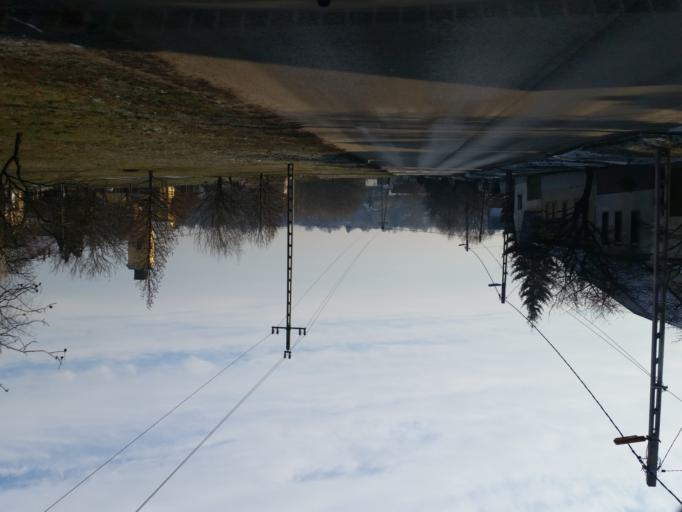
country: HU
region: Pest
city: Biatorbagy
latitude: 47.4796
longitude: 18.8323
